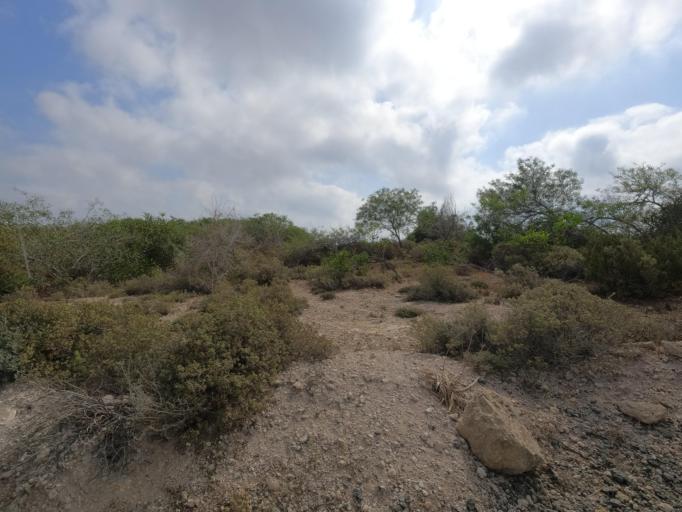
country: CY
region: Ammochostos
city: Ayia Napa
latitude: 35.0107
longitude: 34.0086
